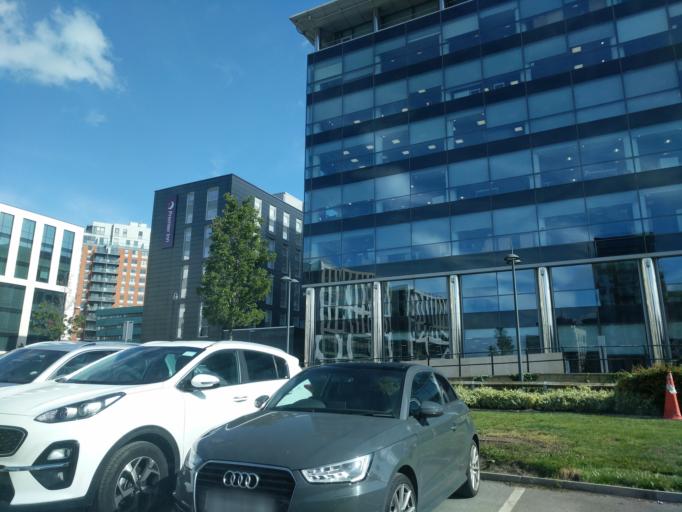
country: GB
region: England
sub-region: City and Borough of Leeds
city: Leeds
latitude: 53.7946
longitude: -1.5542
